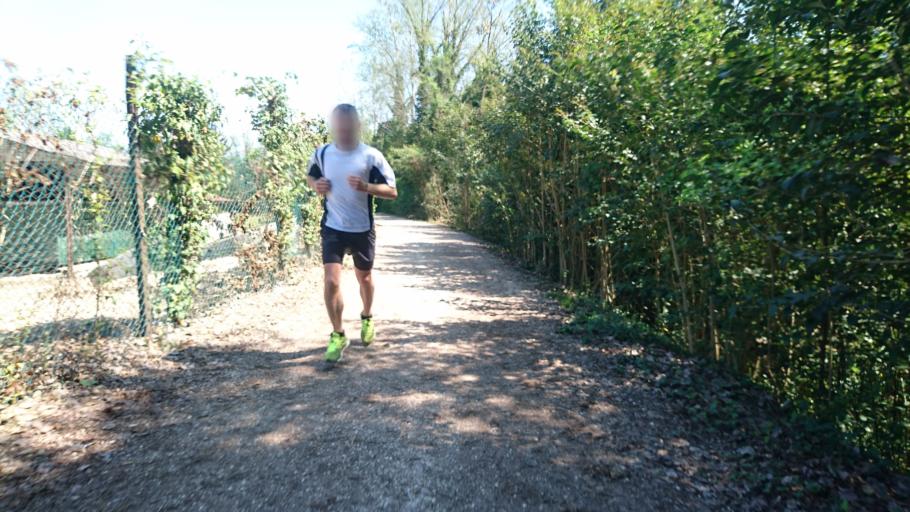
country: IT
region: Veneto
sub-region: Provincia di Treviso
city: Casier
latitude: 45.6436
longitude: 12.2819
